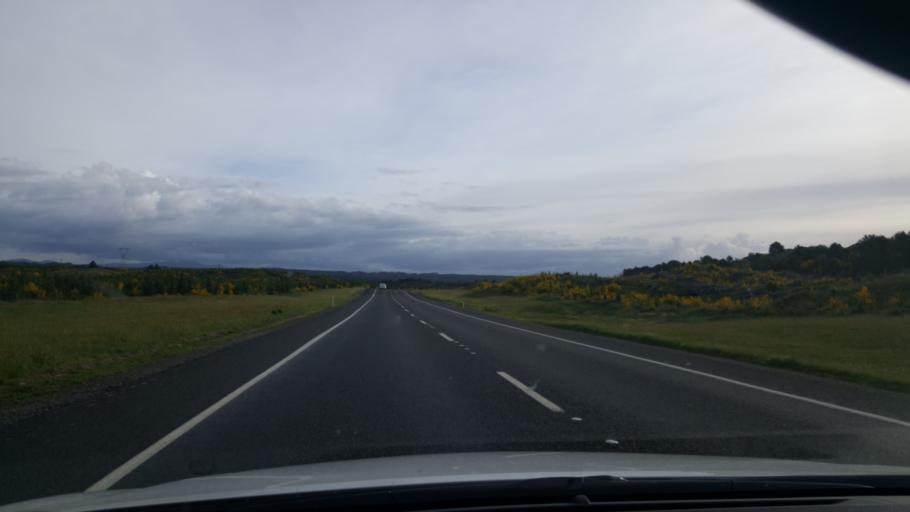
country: NZ
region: Waikato
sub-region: Taupo District
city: Taupo
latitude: -38.8479
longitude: 176.0569
